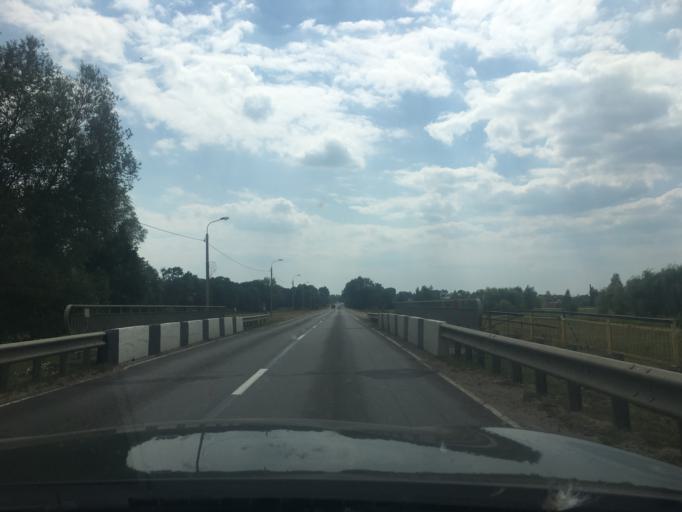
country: BY
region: Brest
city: Pruzhany
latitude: 52.5607
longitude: 24.4797
